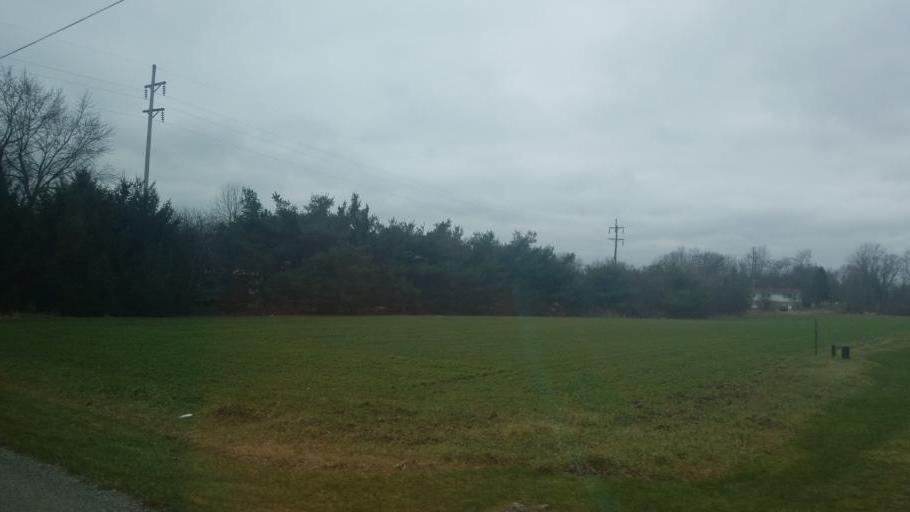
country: US
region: Ohio
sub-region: Crawford County
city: Crestline
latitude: 40.7957
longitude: -82.7323
